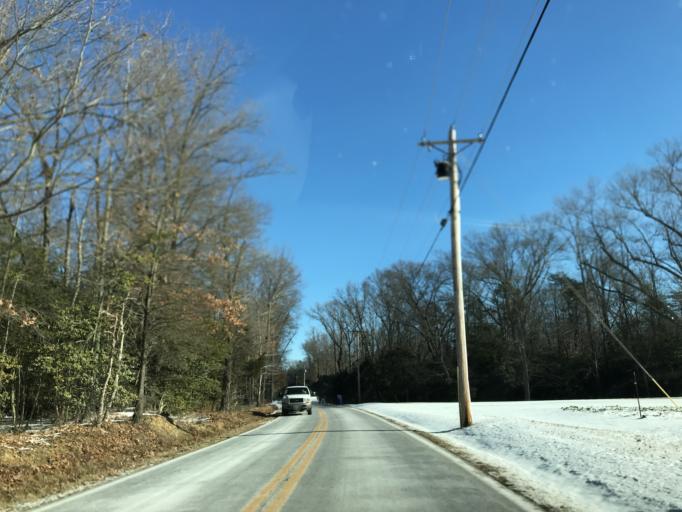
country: US
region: Maryland
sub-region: Charles County
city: La Plata
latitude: 38.4344
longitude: -76.9241
